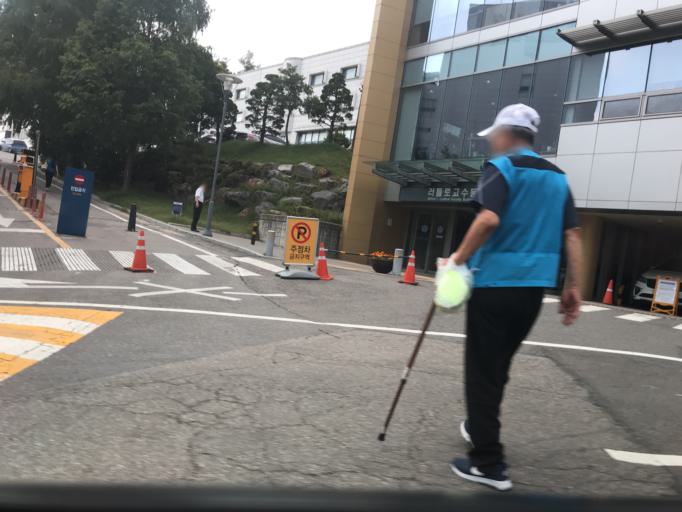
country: KR
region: Seoul
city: Seoul
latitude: 37.5634
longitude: 126.9413
